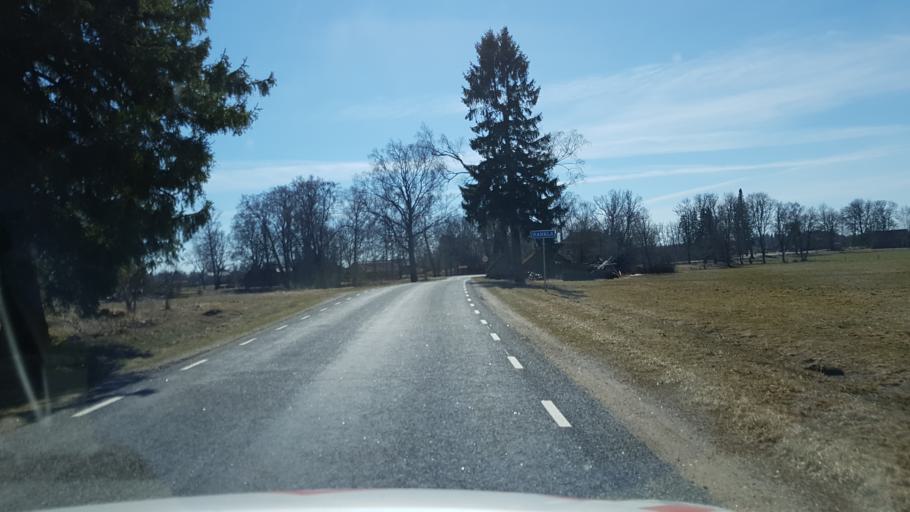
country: EE
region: Laeaene-Virumaa
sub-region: Vinni vald
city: Vinni
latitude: 59.1009
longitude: 26.5264
